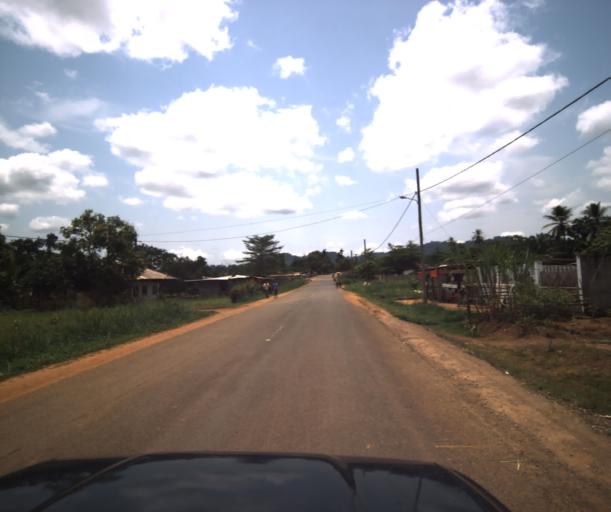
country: CM
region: Centre
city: Eseka
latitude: 3.6468
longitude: 10.7851
